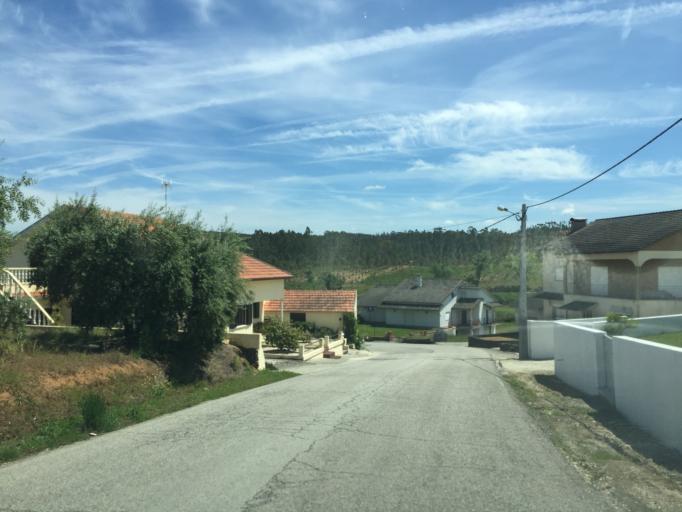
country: PT
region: Coimbra
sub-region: Soure
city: Soure
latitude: 40.0520
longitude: -8.6715
